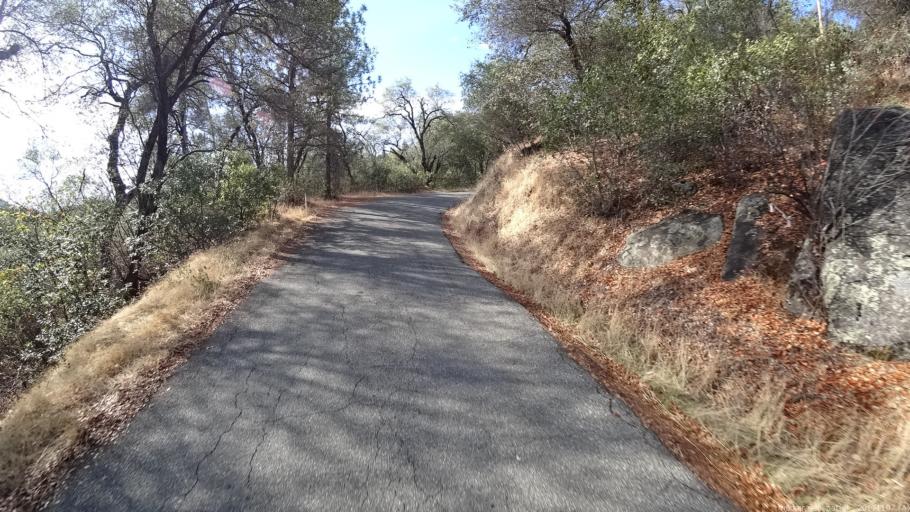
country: US
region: California
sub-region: Shasta County
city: Shasta
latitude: 40.5375
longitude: -122.5594
